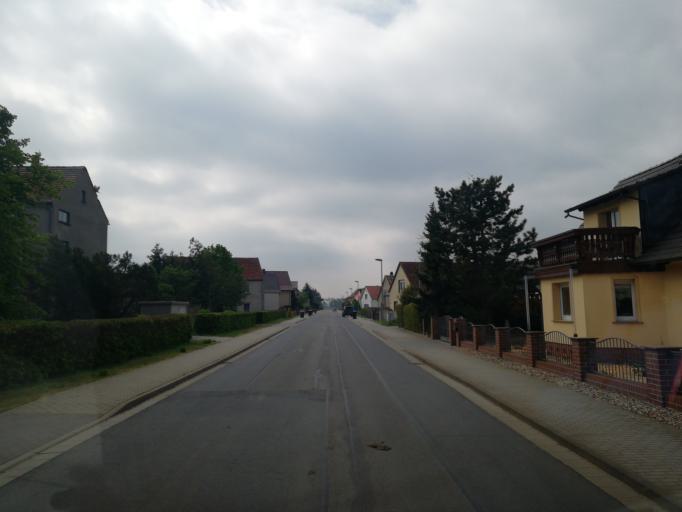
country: DE
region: Saxony
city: Beilrode
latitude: 51.6370
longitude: 13.1201
